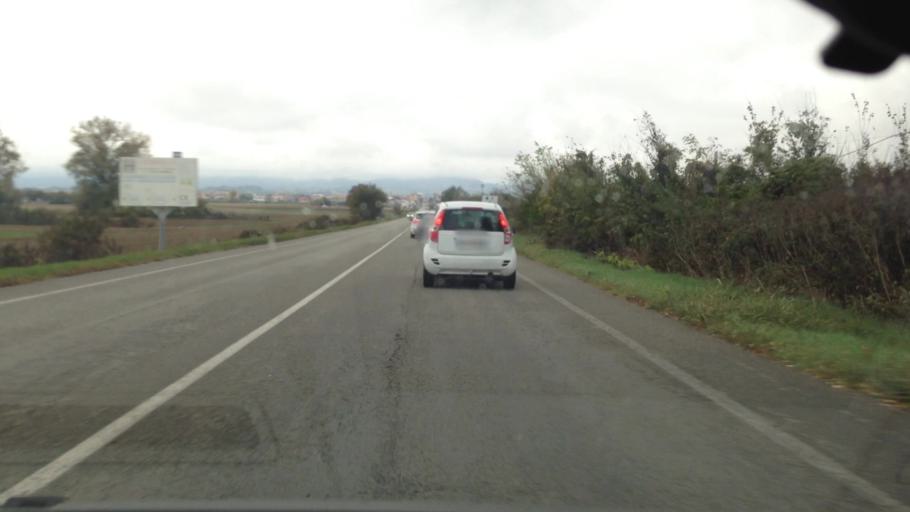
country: IT
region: Piedmont
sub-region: Provincia di Torino
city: Riva Presso Chieri
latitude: 44.9925
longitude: 7.8635
